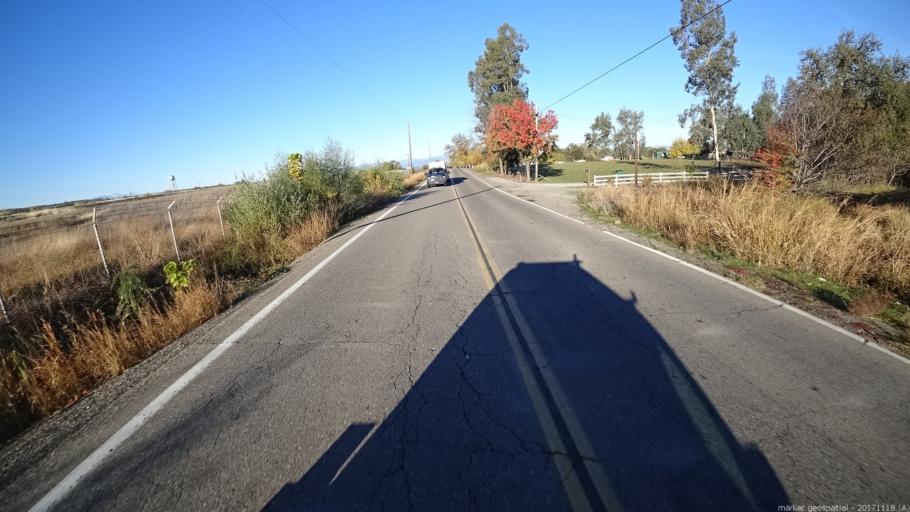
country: US
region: California
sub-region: Shasta County
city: Anderson
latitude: 40.4388
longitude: -122.2712
